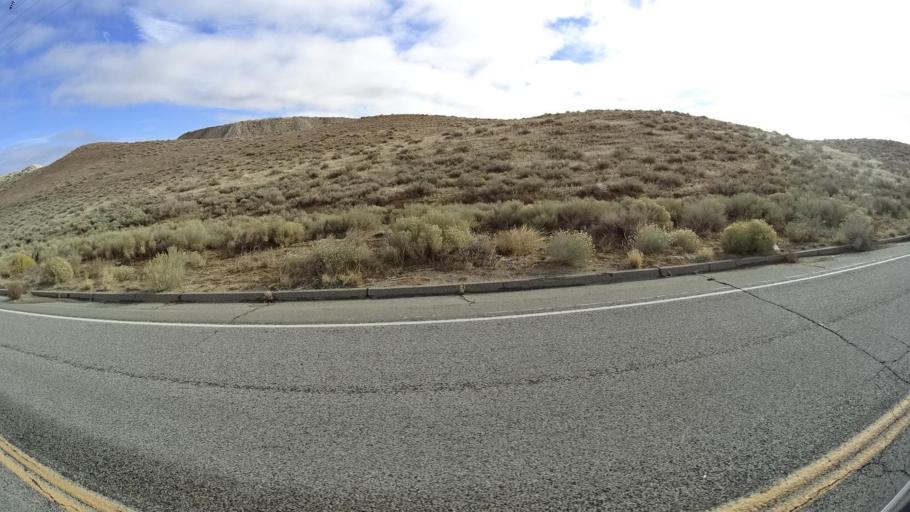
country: US
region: California
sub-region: Kern County
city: Tehachapi
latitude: 35.0432
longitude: -118.3542
